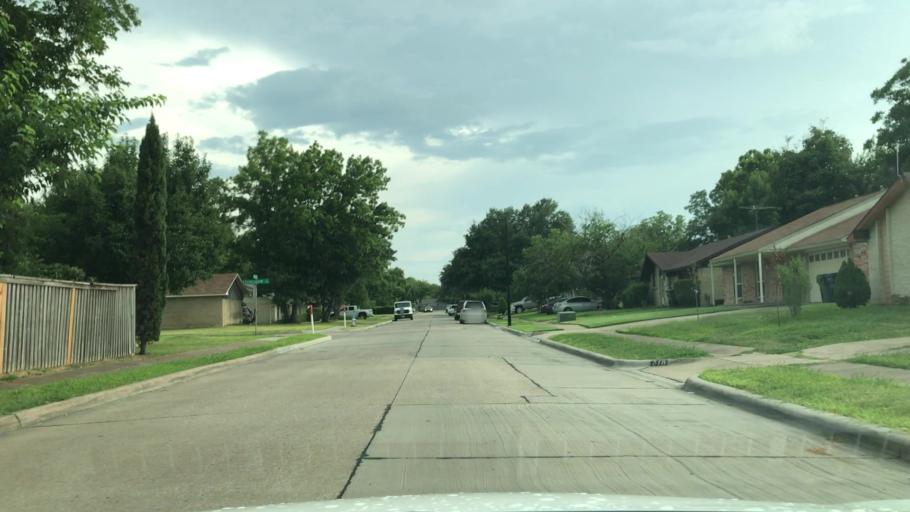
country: US
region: Texas
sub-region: Dallas County
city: Garland
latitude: 32.8599
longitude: -96.6363
